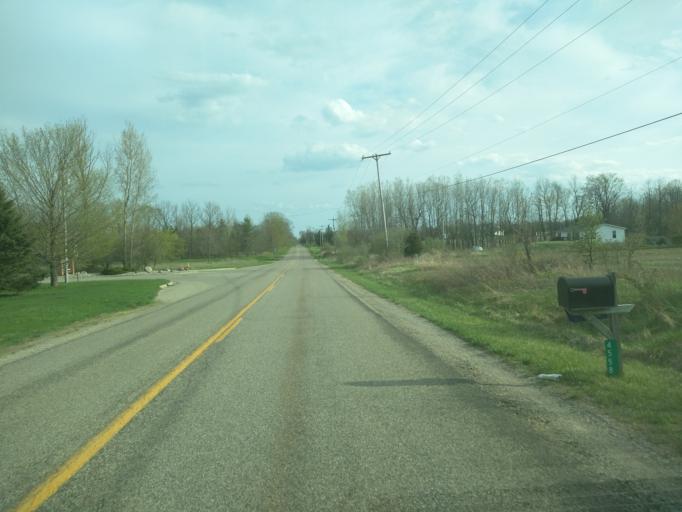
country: US
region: Michigan
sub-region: Eaton County
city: Dimondale
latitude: 42.6342
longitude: -84.6420
